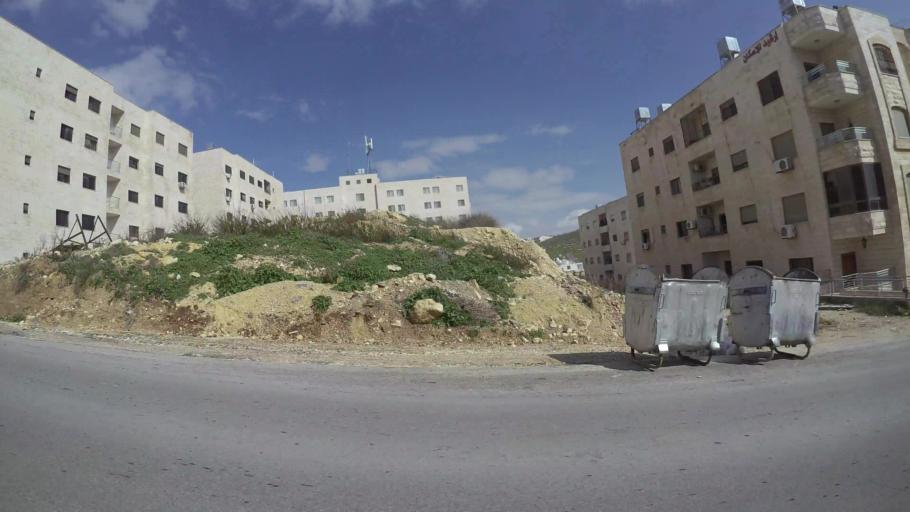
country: JO
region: Amman
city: Al Jubayhah
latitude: 32.0171
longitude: 35.8539
